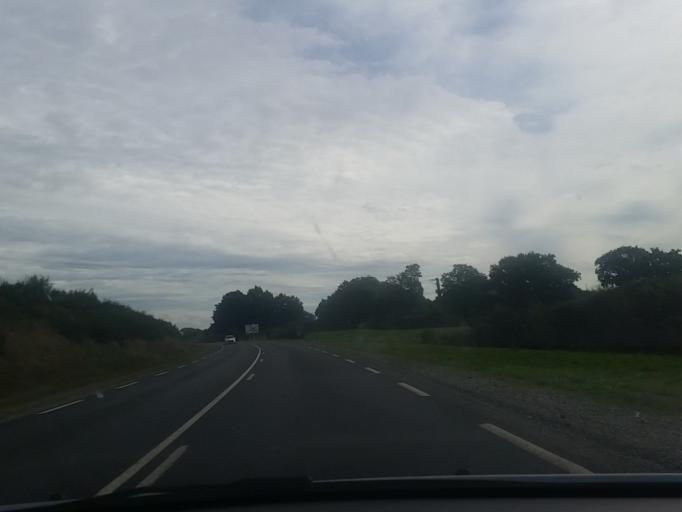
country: FR
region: Pays de la Loire
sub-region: Departement de la Loire-Atlantique
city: Chateaubriant
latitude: 47.6998
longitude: -1.3716
